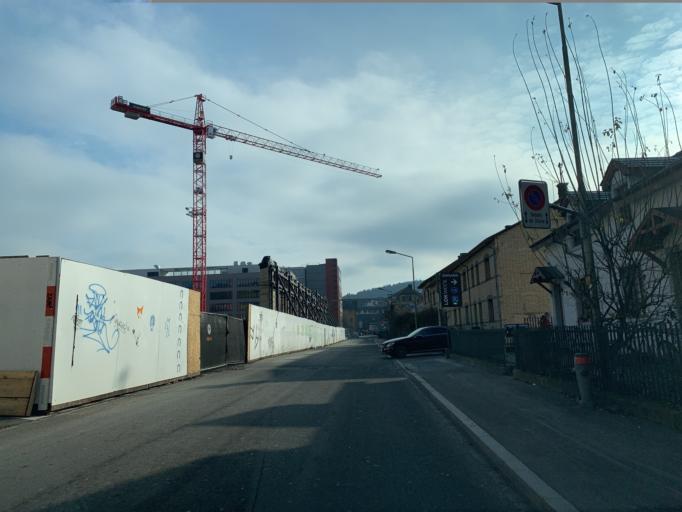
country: CH
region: Zurich
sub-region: Bezirk Winterthur
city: Stadt Winterthur (Kreis 1) / Toessfeld
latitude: 47.4952
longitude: 8.7142
